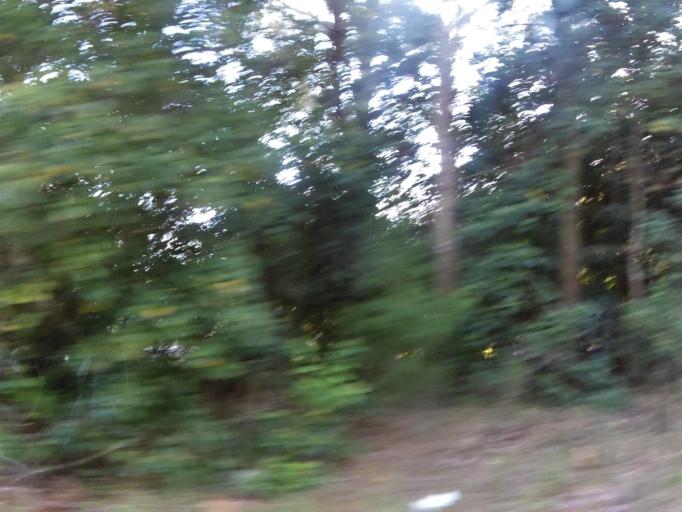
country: US
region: Florida
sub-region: Saint Johns County
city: Fruit Cove
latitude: 30.2005
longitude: -81.5871
